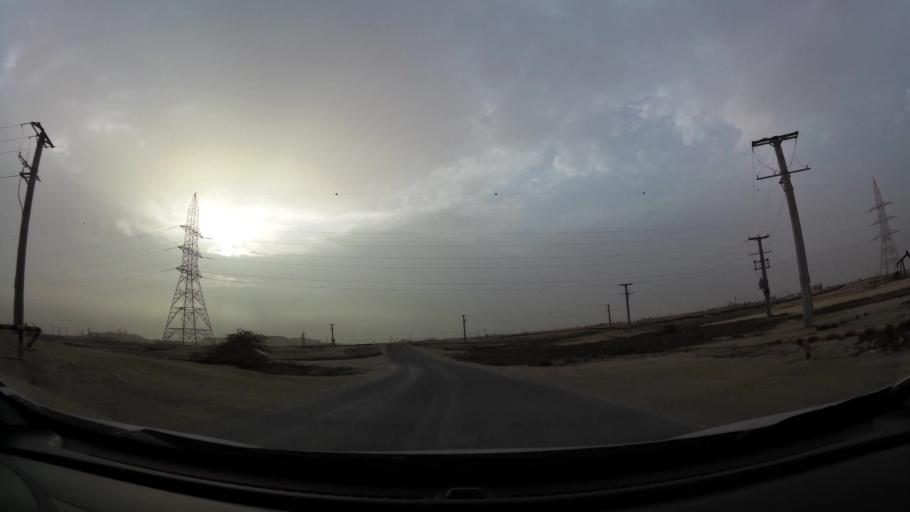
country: BH
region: Central Governorate
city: Dar Kulayb
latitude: 26.0401
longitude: 50.5777
